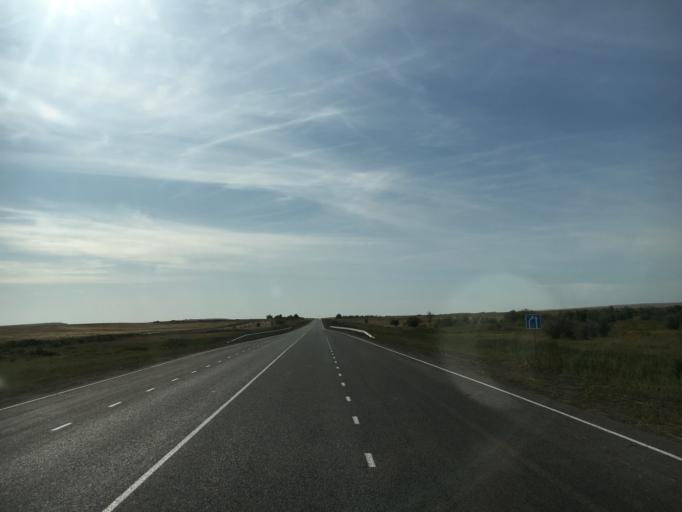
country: KZ
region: Batys Qazaqstan
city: Kamenka
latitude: 51.1071
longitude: 50.4110
